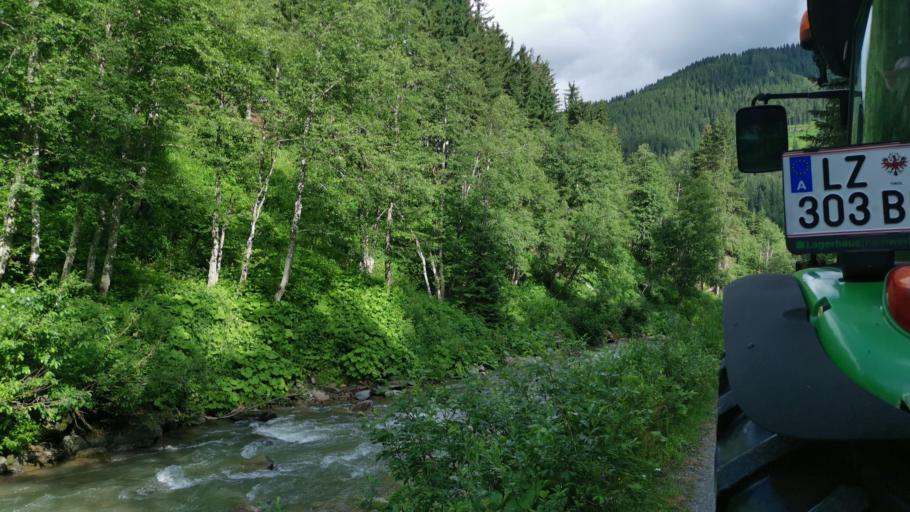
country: AT
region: Tyrol
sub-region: Politischer Bezirk Lienz
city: Obertilliach
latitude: 46.7029
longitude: 12.6050
